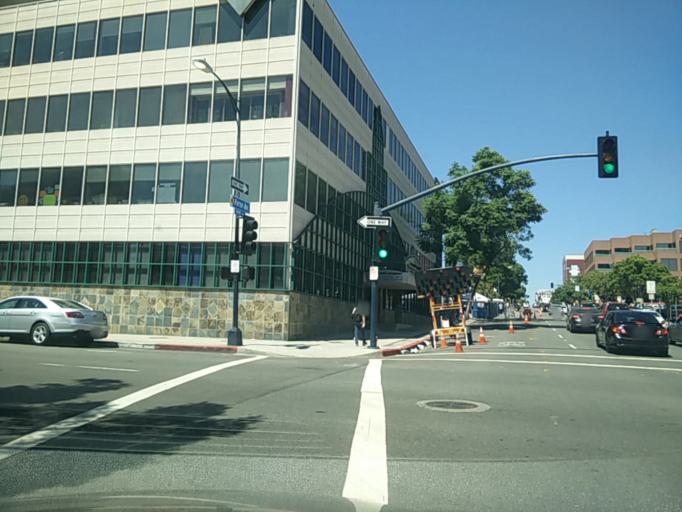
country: US
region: California
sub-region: San Diego County
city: San Diego
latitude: 32.7198
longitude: -117.1602
